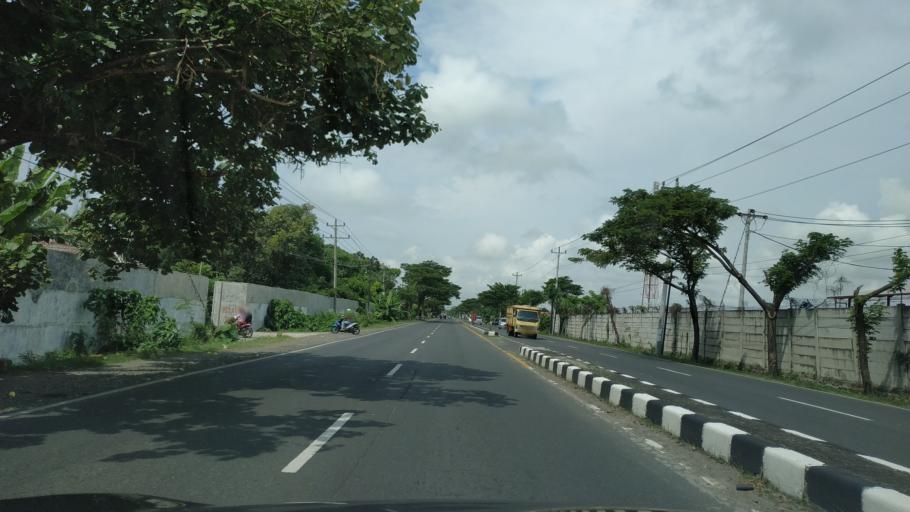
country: ID
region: Central Java
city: Tarub
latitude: -6.8726
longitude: 109.2470
